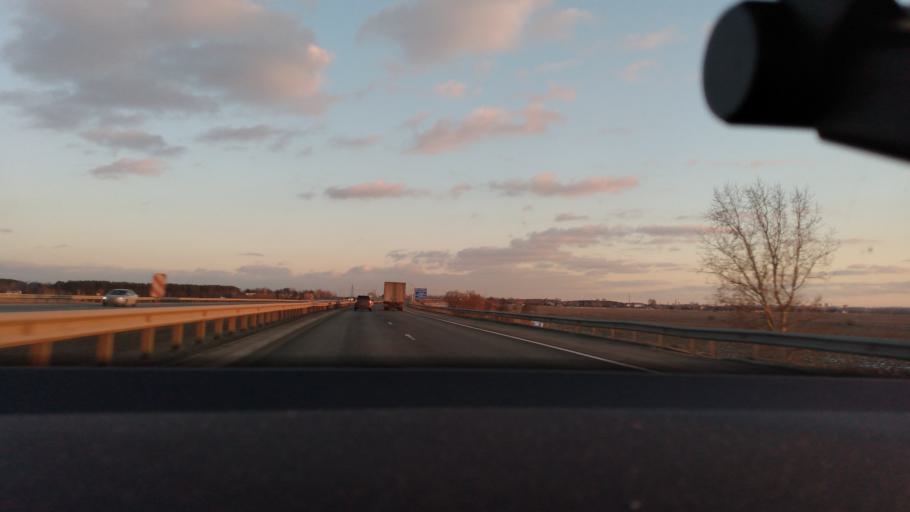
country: RU
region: Moskovskaya
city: Raduzhnyy
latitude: 55.1369
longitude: 38.7663
